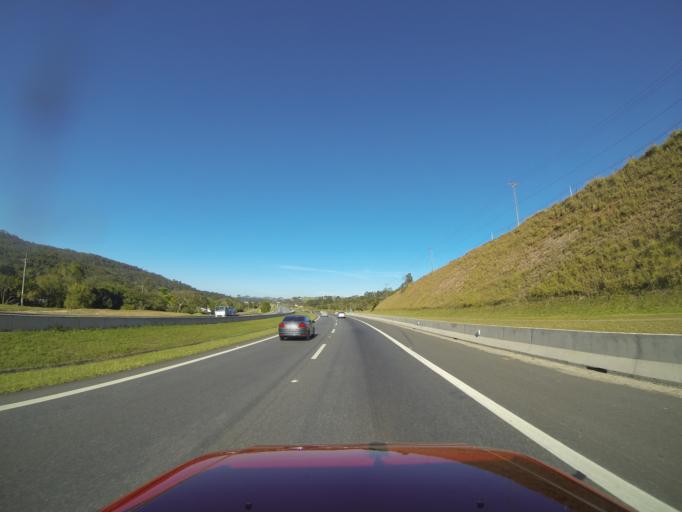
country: BR
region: Sao Paulo
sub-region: Bom Jesus Dos Perdoes
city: Bom Jesus dos Perdoes
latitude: -23.1699
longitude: -46.4408
